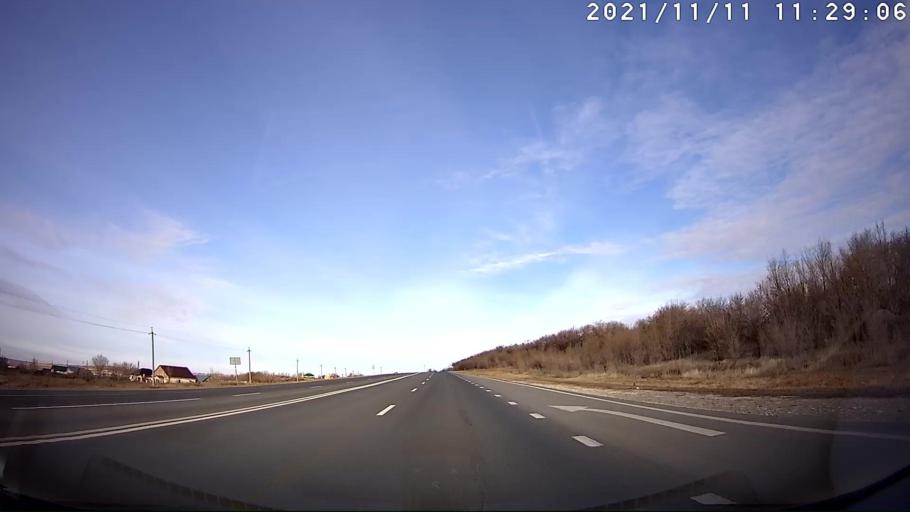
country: RU
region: Samara
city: Varlamovo
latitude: 53.2699
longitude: 48.4802
